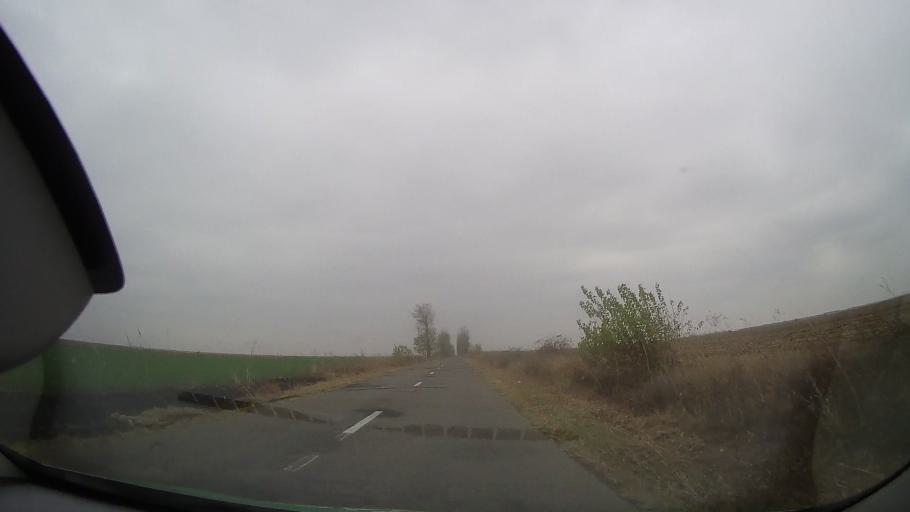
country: RO
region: Ialomita
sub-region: Comuna Grindu
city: Grindu
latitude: 44.7568
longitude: 26.8750
